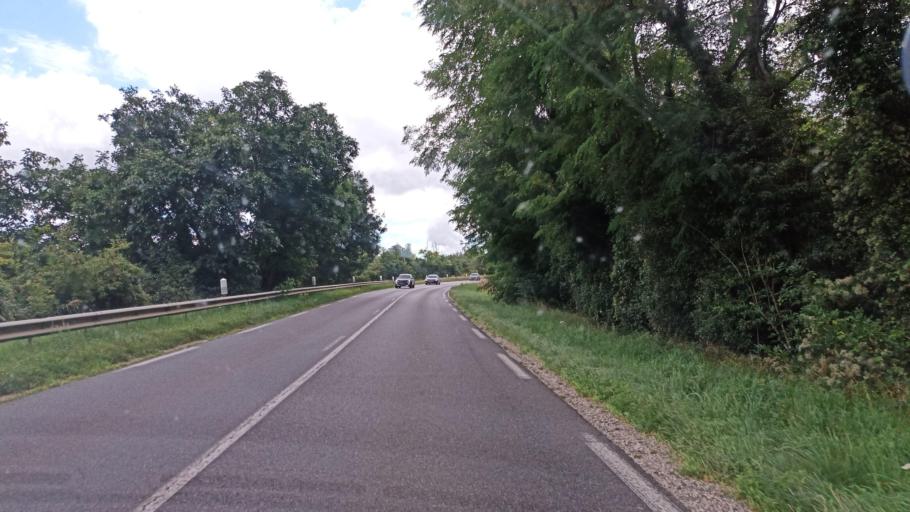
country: FR
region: Ile-de-France
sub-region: Departement de Seine-et-Marne
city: Cannes-Ecluse
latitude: 48.3352
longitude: 2.9582
